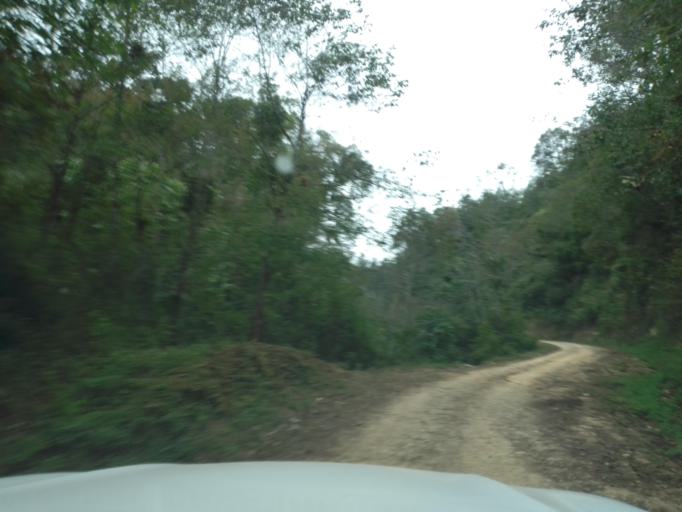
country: GT
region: San Marcos
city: Tacana
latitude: 15.2190
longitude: -92.2143
